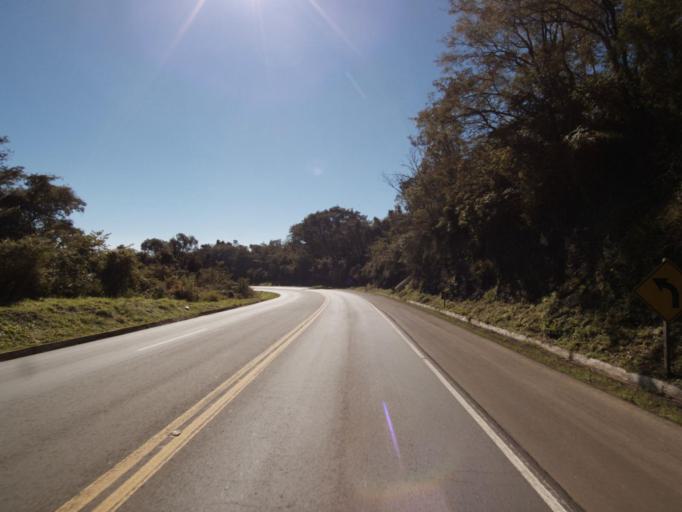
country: BR
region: Santa Catarina
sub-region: Sao Lourenco Do Oeste
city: Sao Lourenco dOeste
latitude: -26.8209
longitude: -53.1813
